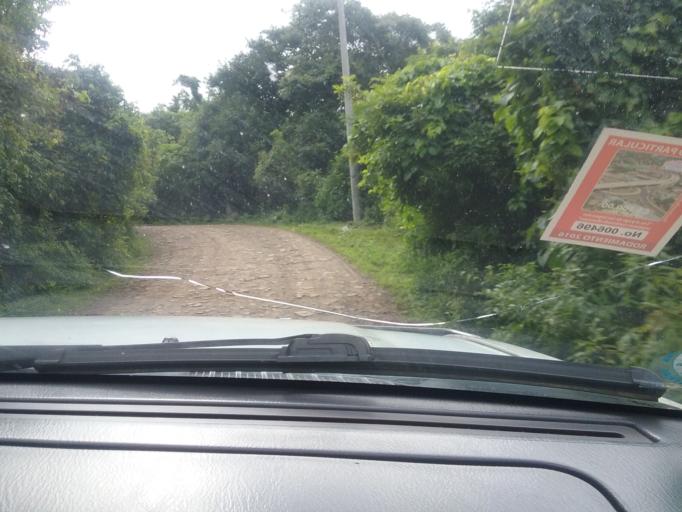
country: NI
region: Matagalpa
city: Matagalpa
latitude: 12.8714
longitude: -85.9503
